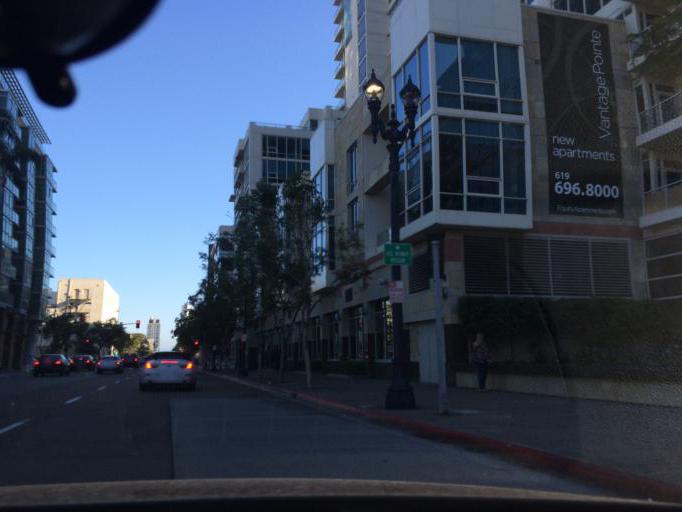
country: US
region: California
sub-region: San Diego County
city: San Diego
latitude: 32.7187
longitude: -117.1557
